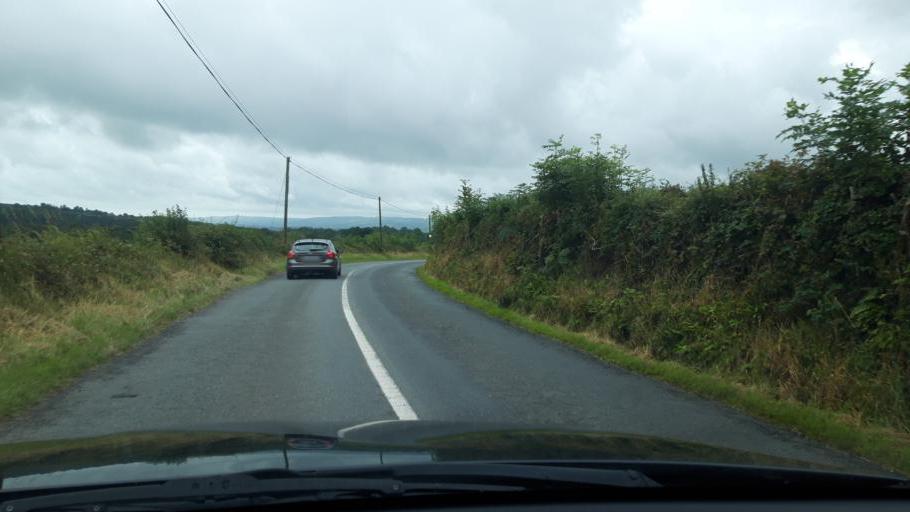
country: IE
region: Munster
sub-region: County Cork
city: Youghal
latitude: 52.1648
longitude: -7.8499
